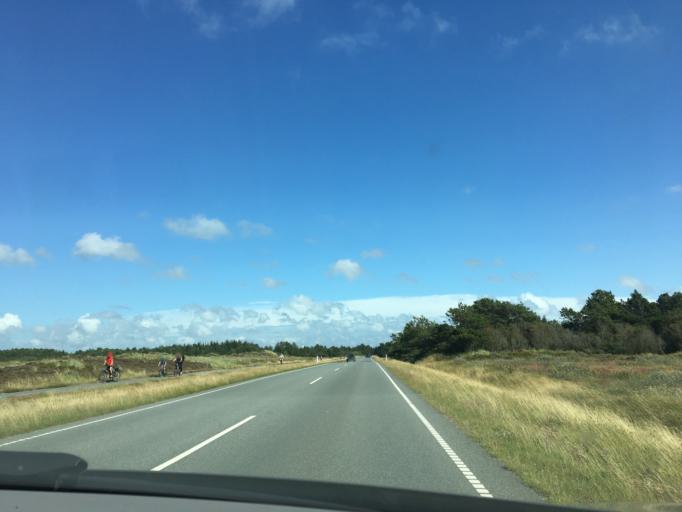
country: DK
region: South Denmark
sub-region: Varde Kommune
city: Oksbol
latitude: 55.7342
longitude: 8.1929
